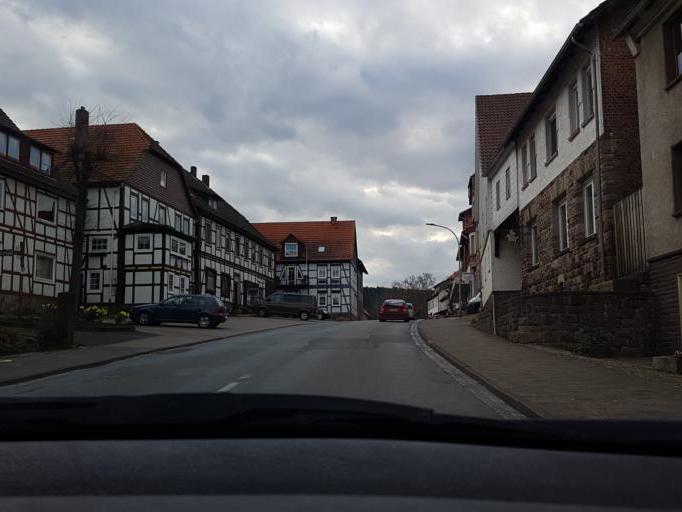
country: DE
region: Lower Saxony
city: Bodenfelde
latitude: 51.6392
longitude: 9.5551
